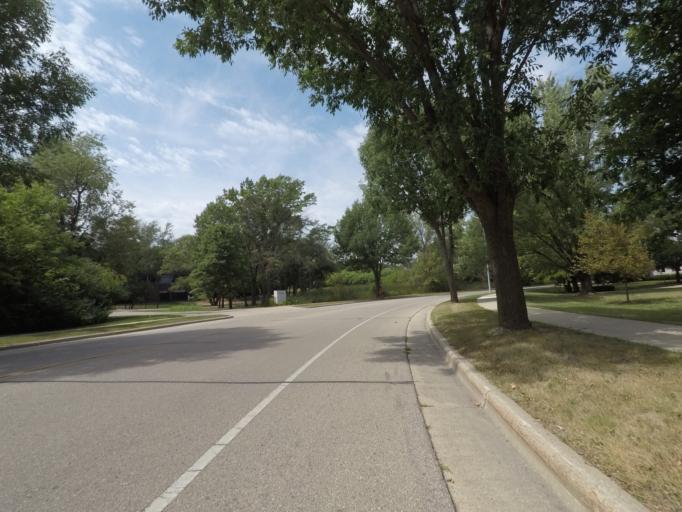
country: US
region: Wisconsin
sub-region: Dane County
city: Middleton
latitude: 43.0799
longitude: -89.5339
